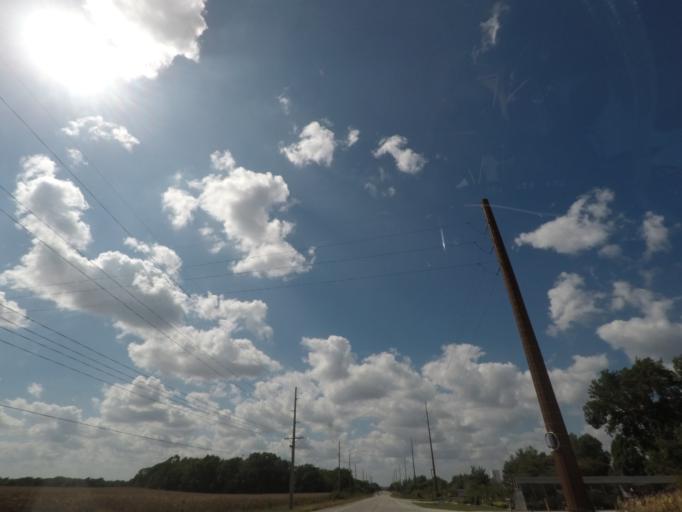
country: US
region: Iowa
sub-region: Story County
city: Ames
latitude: 42.0230
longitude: -93.5600
